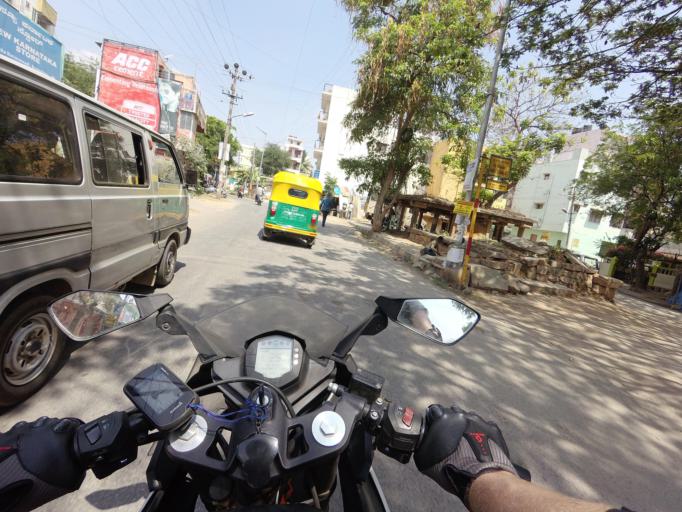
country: IN
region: Karnataka
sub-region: Bangalore Urban
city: Bangalore
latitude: 13.0063
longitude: 77.6473
